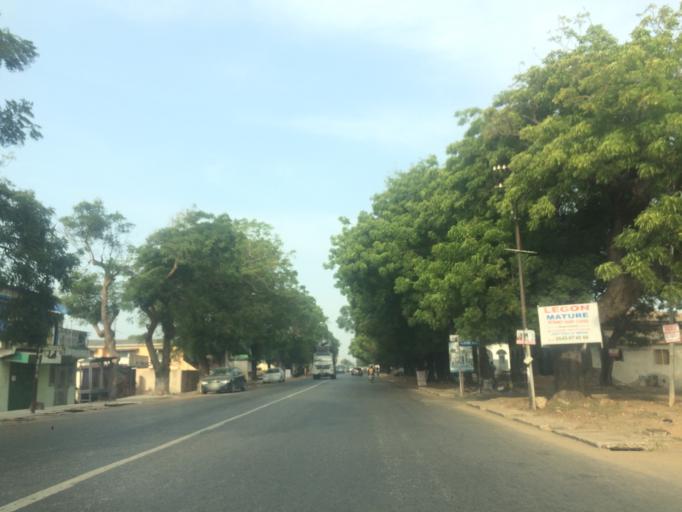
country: GH
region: Greater Accra
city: Accra
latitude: 5.5367
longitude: -0.2241
